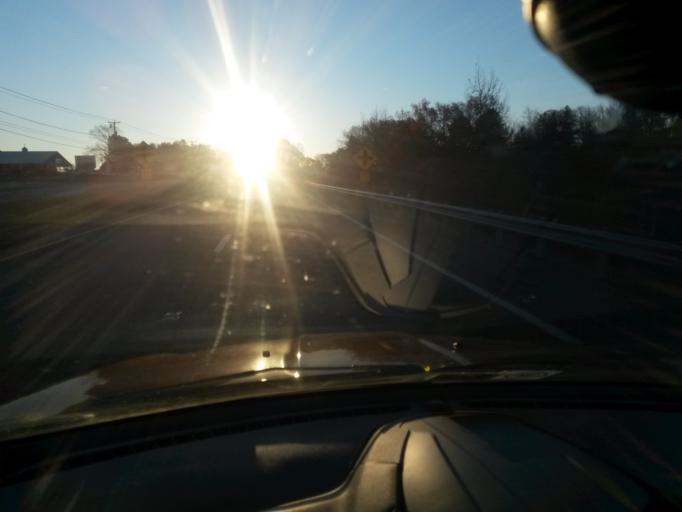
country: US
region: Virginia
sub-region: Franklin County
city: Rocky Mount
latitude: 37.0677
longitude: -79.8900
